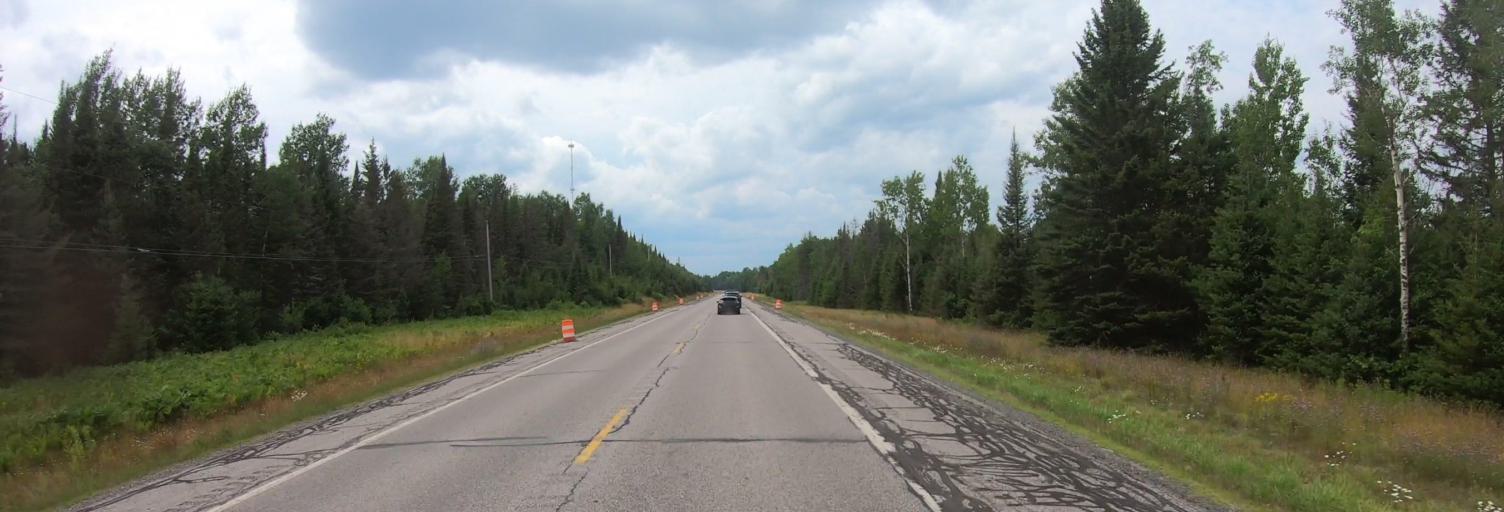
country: US
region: Michigan
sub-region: Baraga County
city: L'Anse
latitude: 46.5669
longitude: -88.2505
